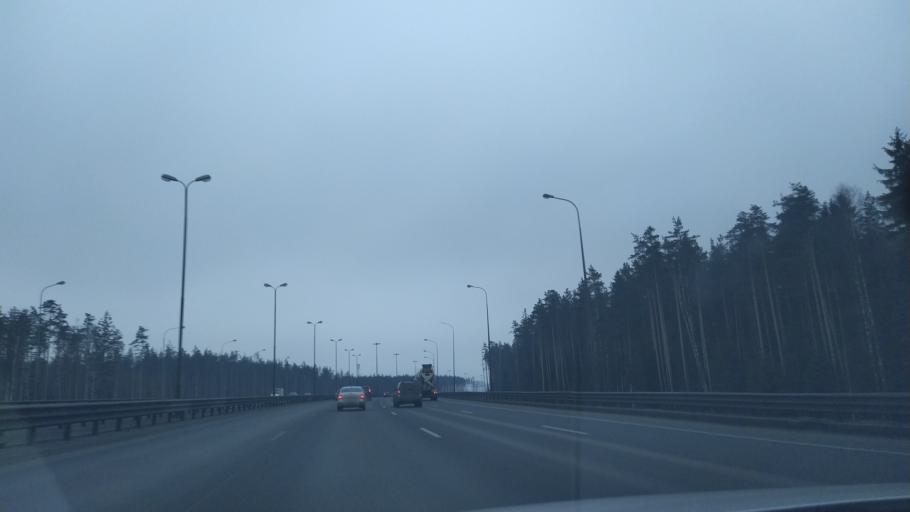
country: RU
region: Leningrad
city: Yanino Vtoroye
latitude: 59.9661
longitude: 30.5527
